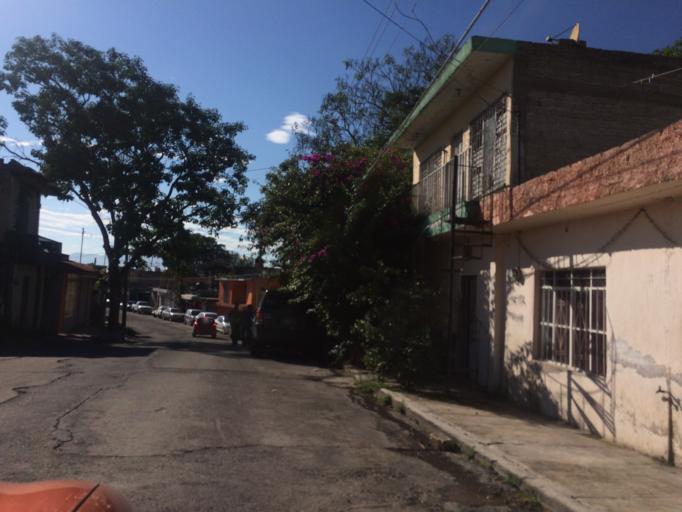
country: MX
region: Nayarit
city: Tepic
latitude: 21.4996
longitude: -104.9137
